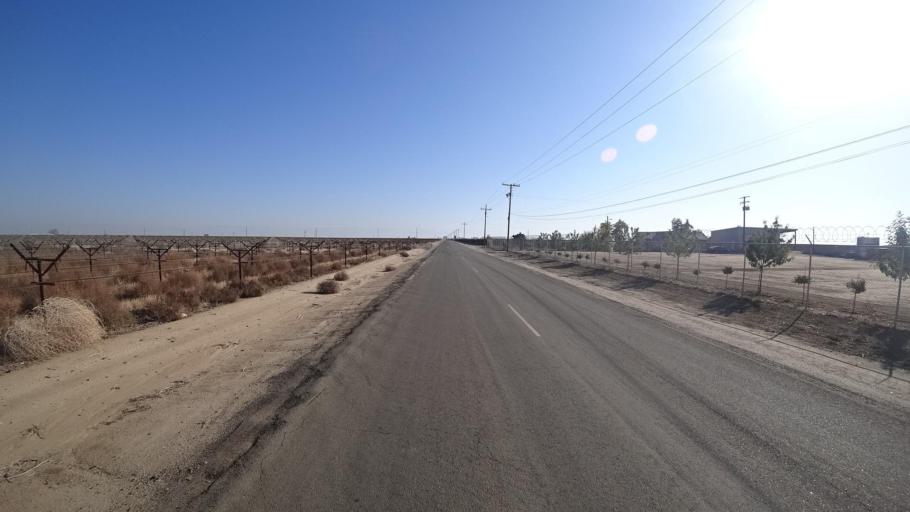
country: US
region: California
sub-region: Kern County
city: Delano
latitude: 35.7469
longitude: -119.2108
